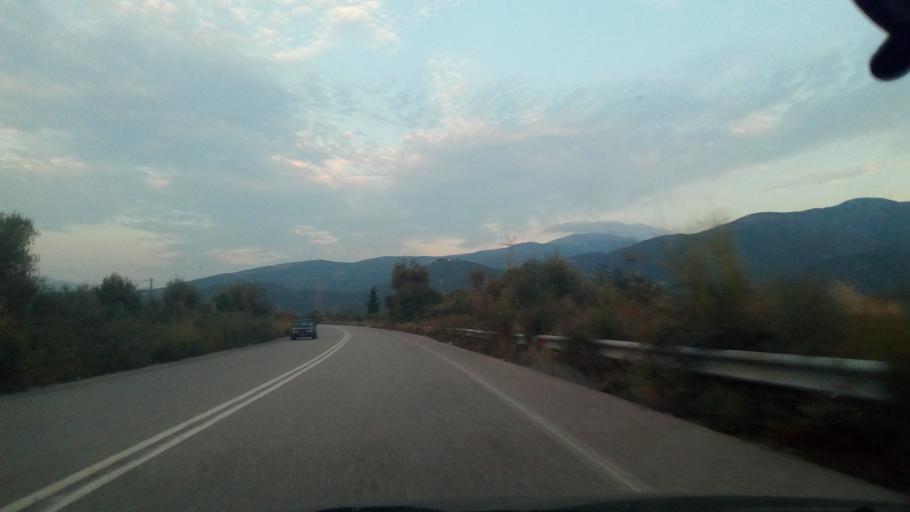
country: GR
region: West Greece
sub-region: Nomos Aitolias kai Akarnanias
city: Nafpaktos
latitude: 38.4106
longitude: 21.8945
